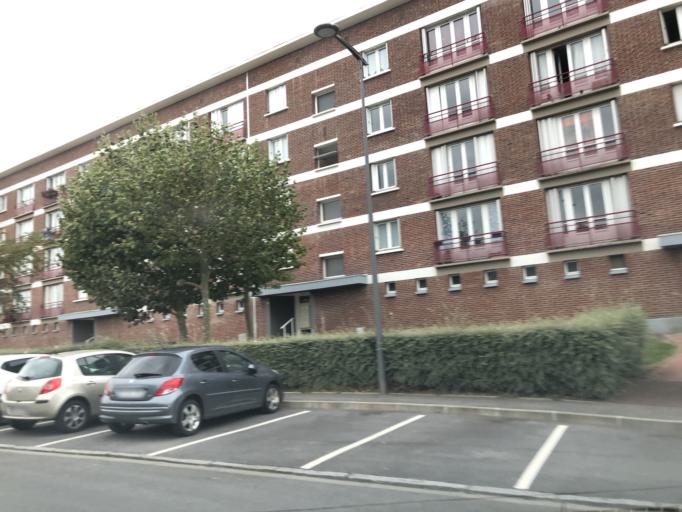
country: FR
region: Haute-Normandie
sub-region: Departement de la Seine-Maritime
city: Rouxmesnil-Bouteilles
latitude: 49.9146
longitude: 1.0776
